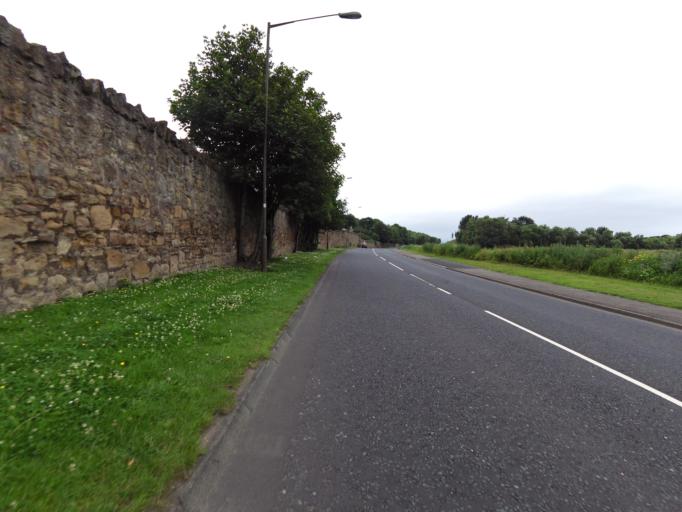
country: GB
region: Scotland
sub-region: East Lothian
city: Prestonpans
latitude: 55.9549
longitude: -2.9977
